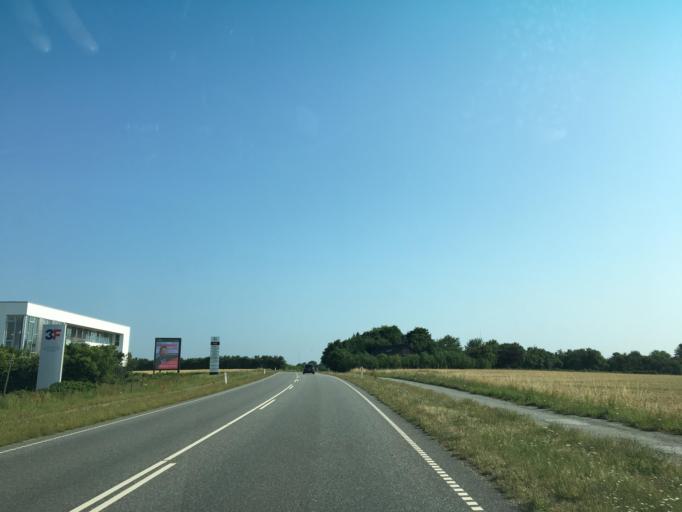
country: DK
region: North Denmark
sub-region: Thisted Kommune
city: Thisted
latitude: 56.9380
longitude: 8.6486
